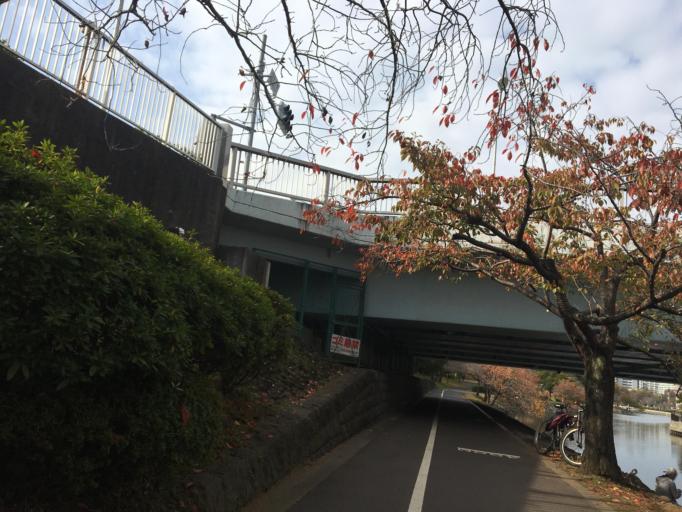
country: JP
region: Tokyo
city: Urayasu
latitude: 35.6533
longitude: 139.8638
